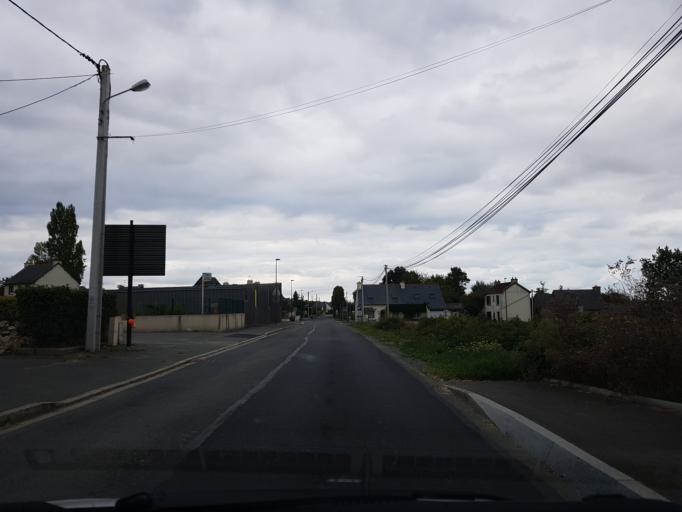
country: FR
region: Brittany
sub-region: Departement des Cotes-d'Armor
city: Langueux
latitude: 48.4646
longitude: -2.7128
